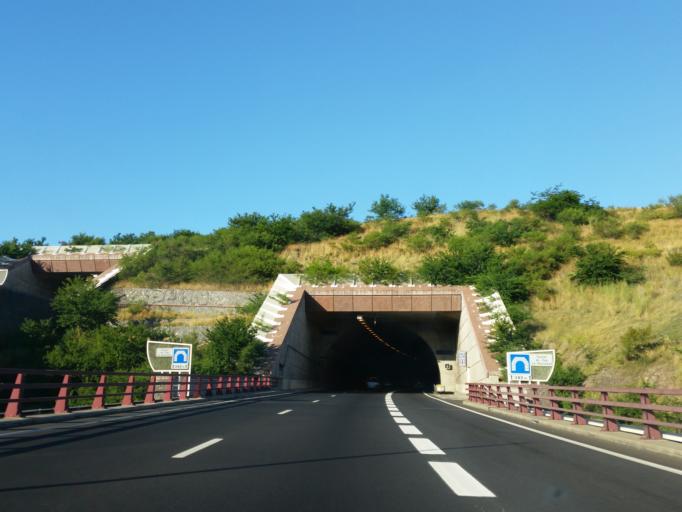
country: RE
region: Reunion
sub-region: Reunion
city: Saint-Paul
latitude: -21.0277
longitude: 55.2552
